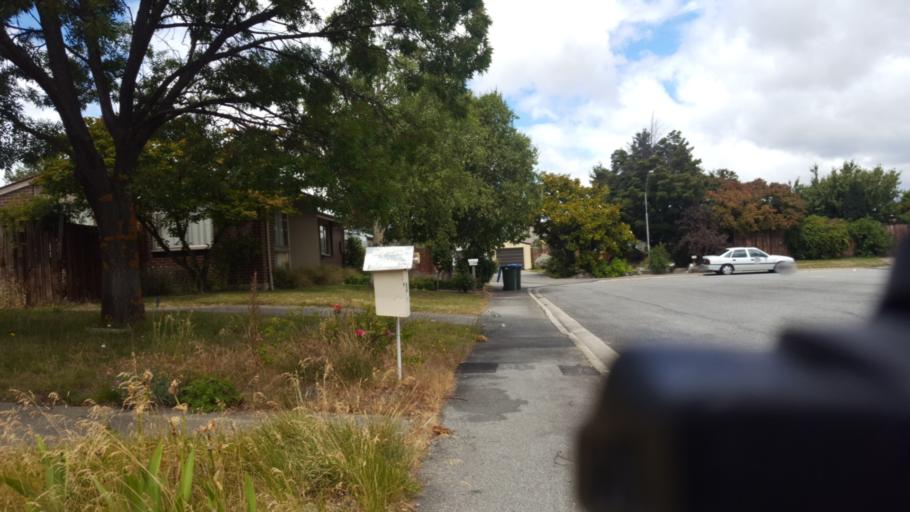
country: NZ
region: Otago
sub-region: Queenstown-Lakes District
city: Wanaka
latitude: -45.0405
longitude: 169.1836
